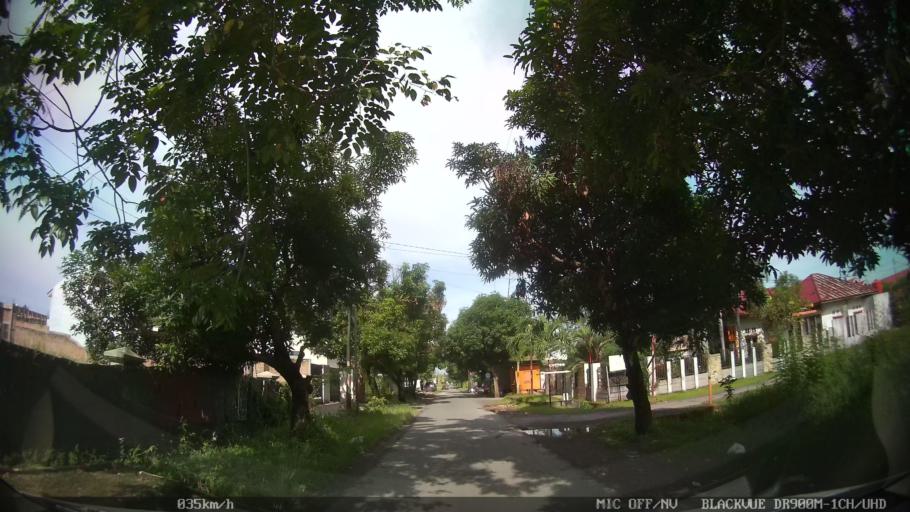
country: ID
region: North Sumatra
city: Medan
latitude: 3.6171
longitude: 98.6610
